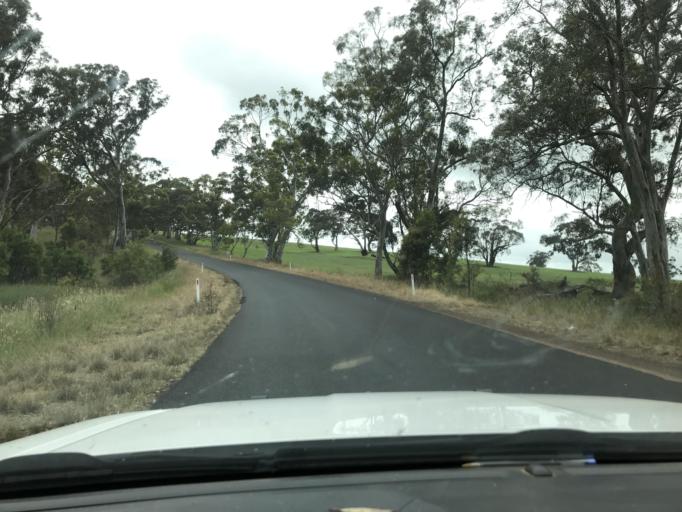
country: AU
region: Victoria
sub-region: Southern Grampians
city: Hamilton
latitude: -37.1899
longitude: 141.5503
